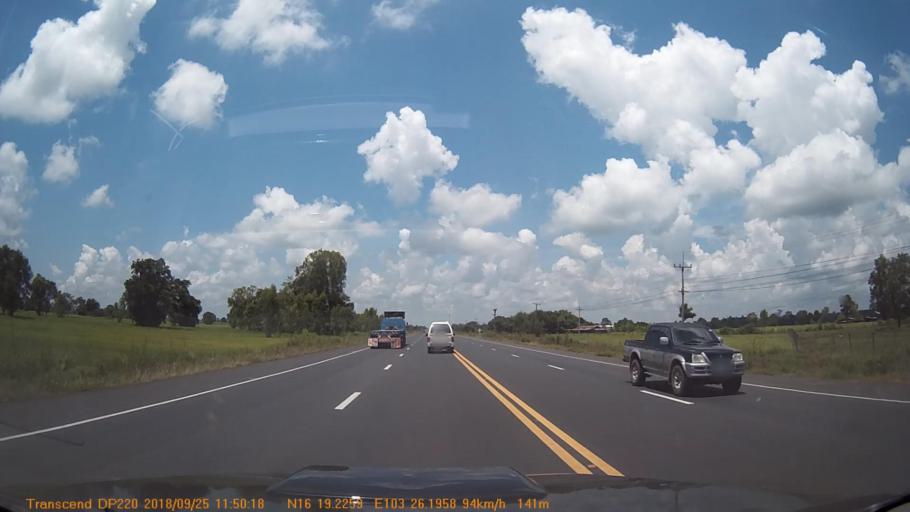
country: TH
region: Kalasin
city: Khong Chai
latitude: 16.3204
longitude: 103.4367
